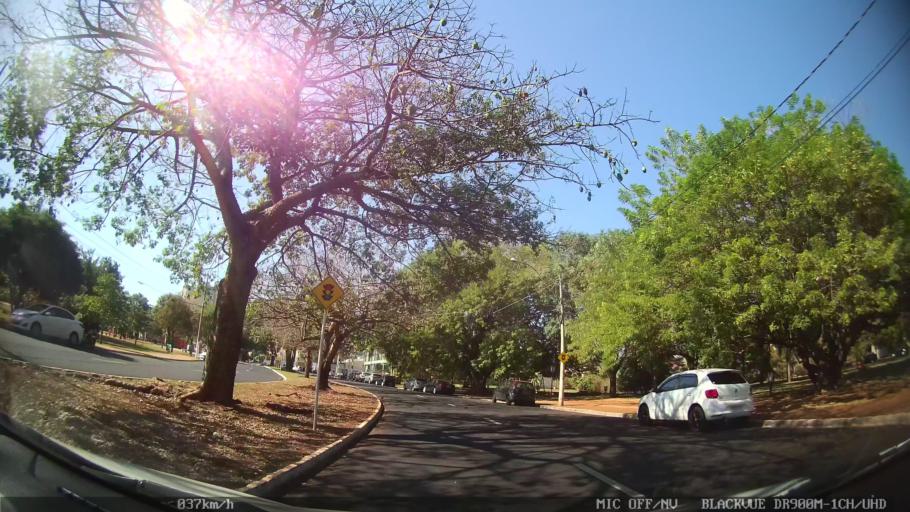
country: BR
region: Sao Paulo
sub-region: Ribeirao Preto
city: Ribeirao Preto
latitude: -21.2117
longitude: -47.8101
